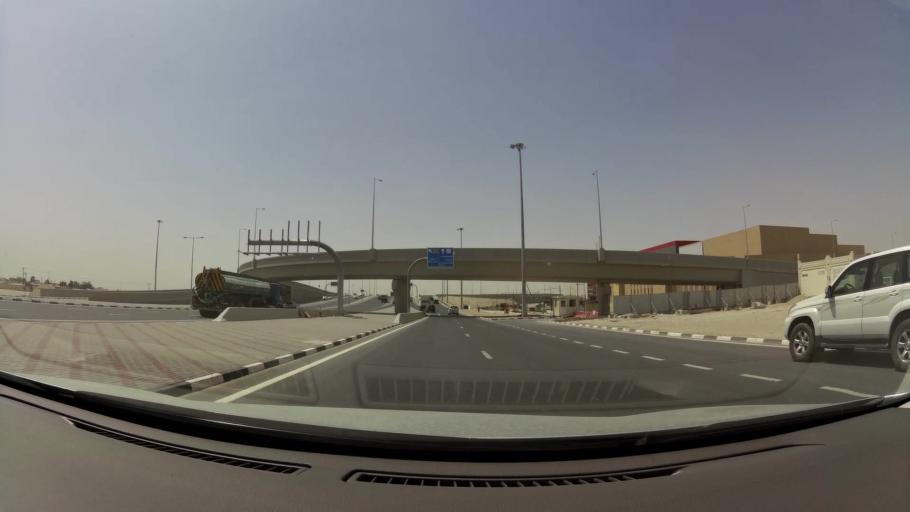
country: QA
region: Baladiyat Umm Salal
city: Umm Salal Muhammad
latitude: 25.3831
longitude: 51.4468
